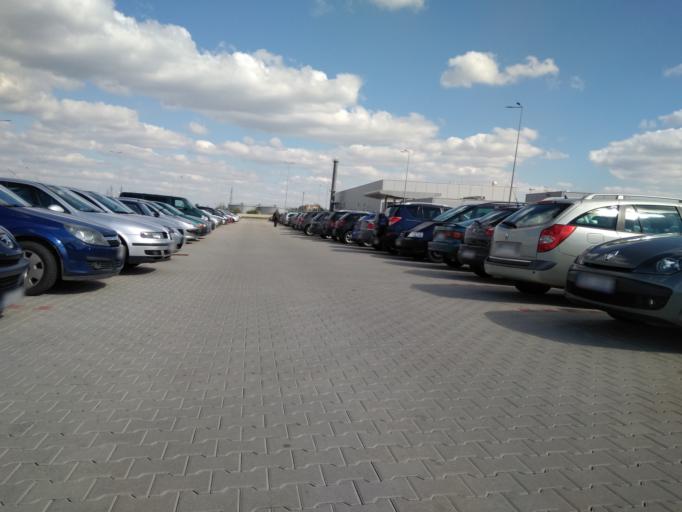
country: PL
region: Greater Poland Voivodeship
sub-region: Powiat wrzesinski
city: Wrzesnia
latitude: 52.2974
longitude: 17.5113
